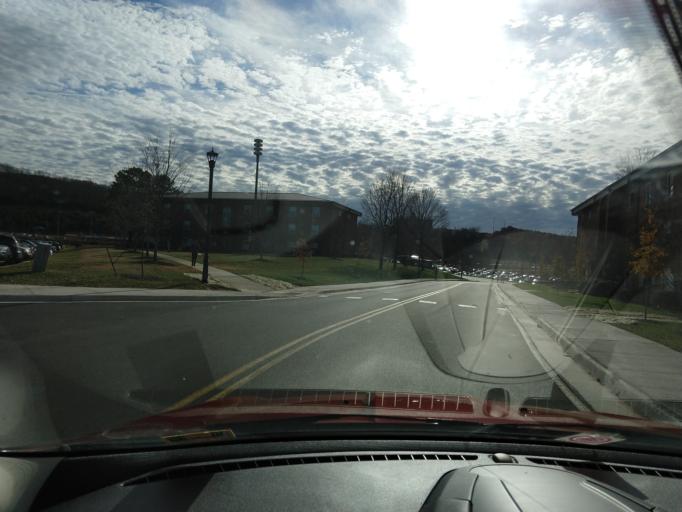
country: US
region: Virginia
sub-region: City of Lynchburg
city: West Lynchburg
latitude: 37.3453
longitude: -79.1849
